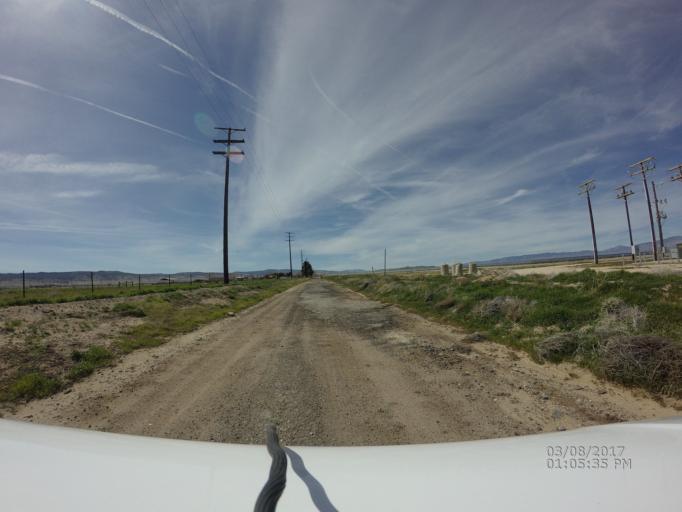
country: US
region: California
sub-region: Los Angeles County
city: Leona Valley
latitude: 34.7184
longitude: -118.2943
